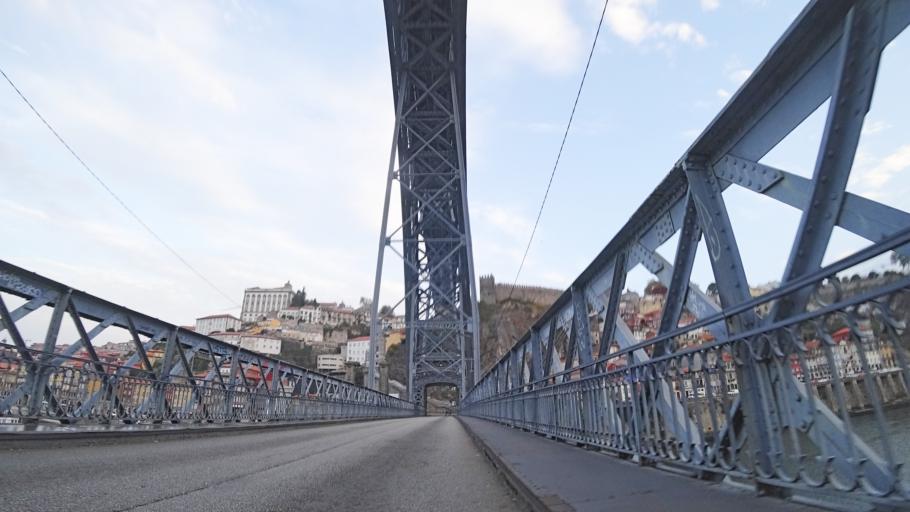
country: PT
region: Porto
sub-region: Porto
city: Porto
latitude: 41.1397
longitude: -8.6093
